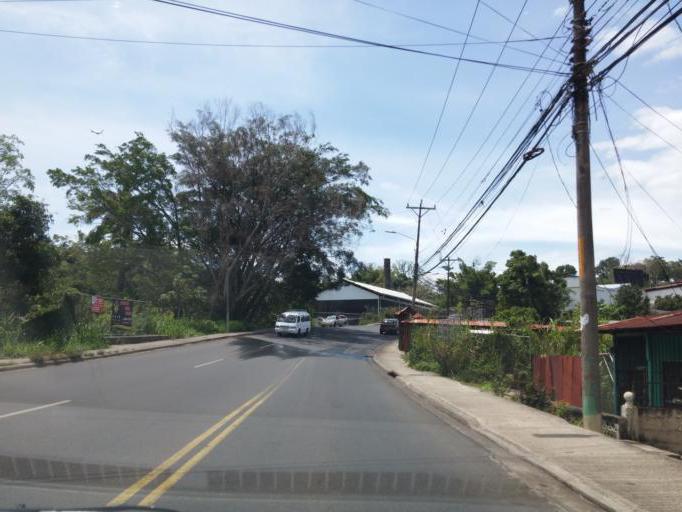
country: CR
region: Alajuela
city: Alajuela
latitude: 10.0034
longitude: -84.2022
